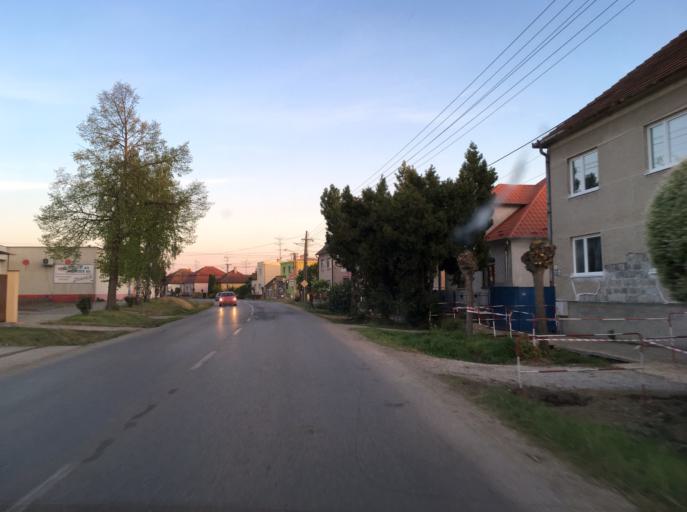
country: SK
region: Nitriansky
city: Kolarovo
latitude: 47.9126
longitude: 18.0007
